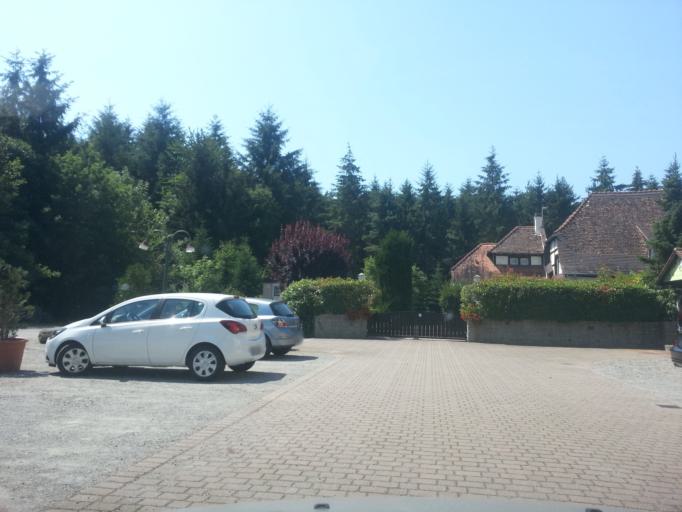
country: DE
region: Hesse
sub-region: Regierungsbezirk Darmstadt
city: Gross-Rohrheim
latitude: 49.7046
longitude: 8.5119
